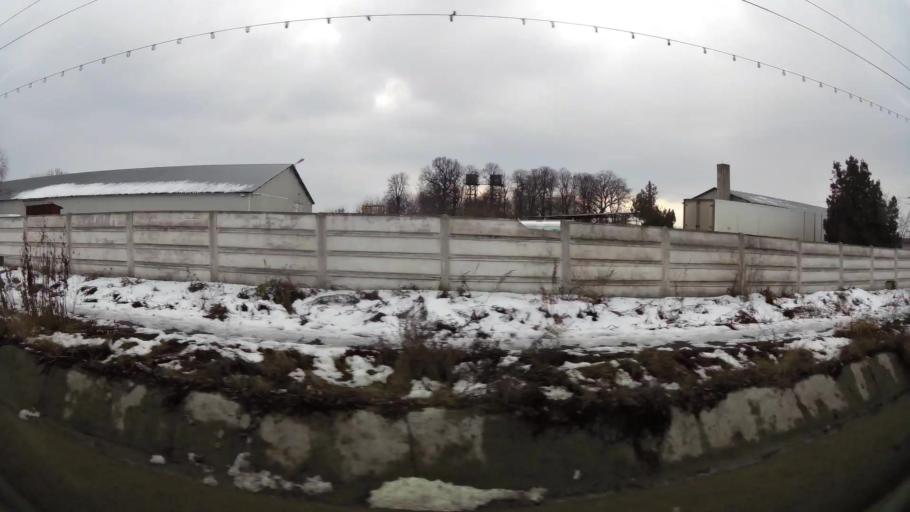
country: RO
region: Ilfov
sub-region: Comuna Afumati
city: Afumati
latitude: 44.5281
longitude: 26.2409
